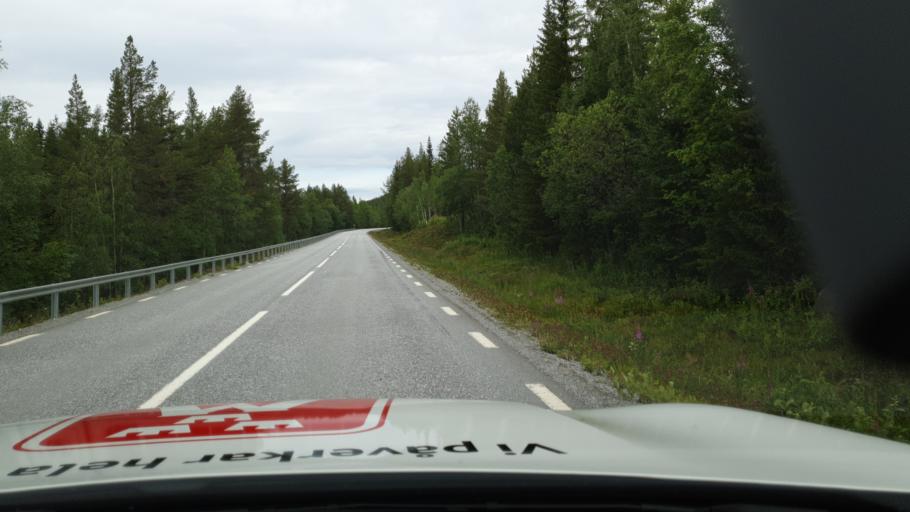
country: SE
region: Vaesterbotten
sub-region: Storumans Kommun
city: Storuman
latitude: 65.1521
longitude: 17.0679
